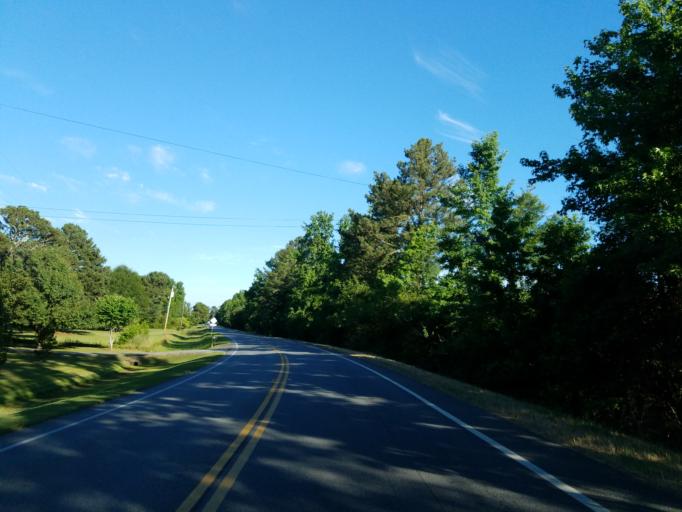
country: US
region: Georgia
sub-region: Gordon County
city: Calhoun
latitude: 34.5445
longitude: -85.0019
